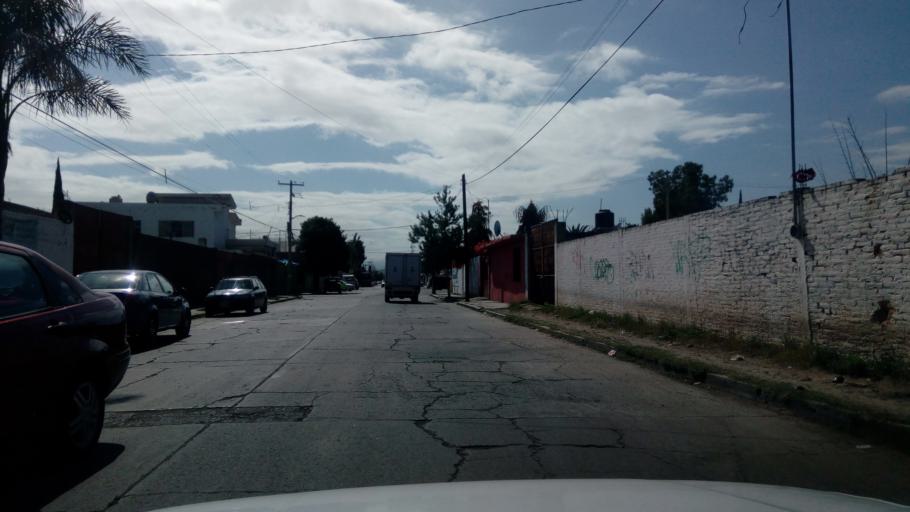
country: MX
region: Durango
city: Victoria de Durango
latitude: 24.0040
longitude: -104.6602
